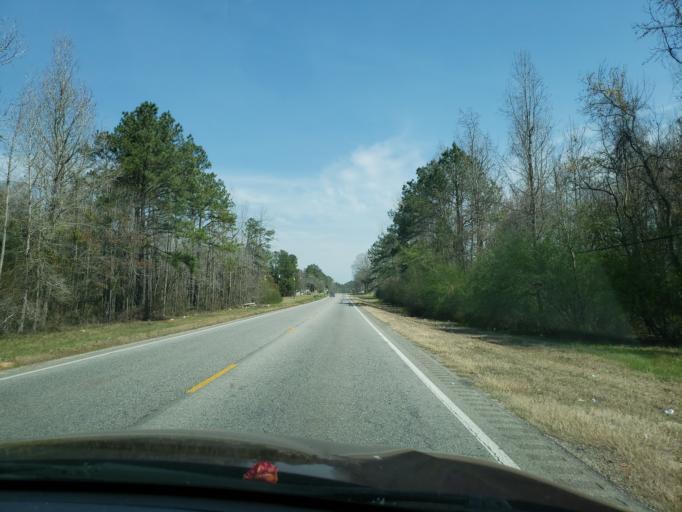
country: US
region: Alabama
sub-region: Elmore County
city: Elmore
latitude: 32.5458
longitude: -86.3000
